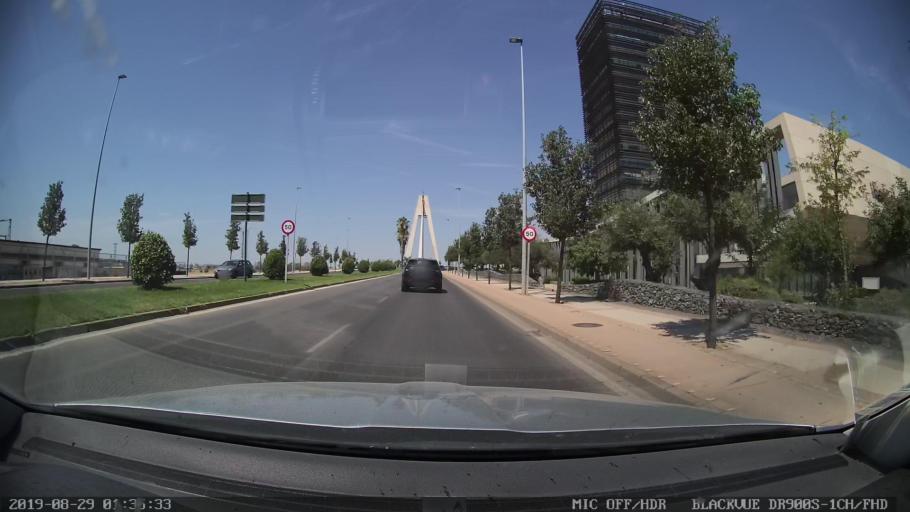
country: ES
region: Extremadura
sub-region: Provincia de Badajoz
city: Badajoz
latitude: 38.8729
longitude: -6.9904
